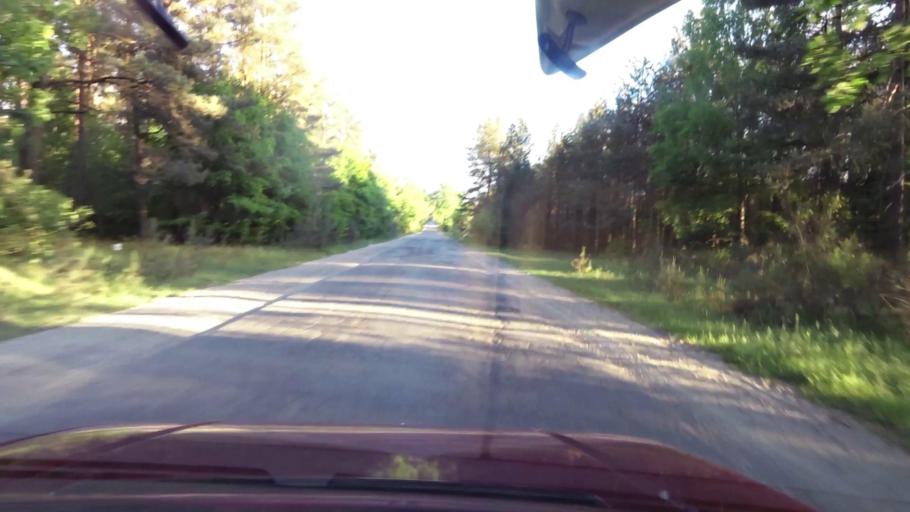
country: PL
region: West Pomeranian Voivodeship
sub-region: Powiat szczecinecki
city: Bialy Bor
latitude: 53.9212
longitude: 16.8046
